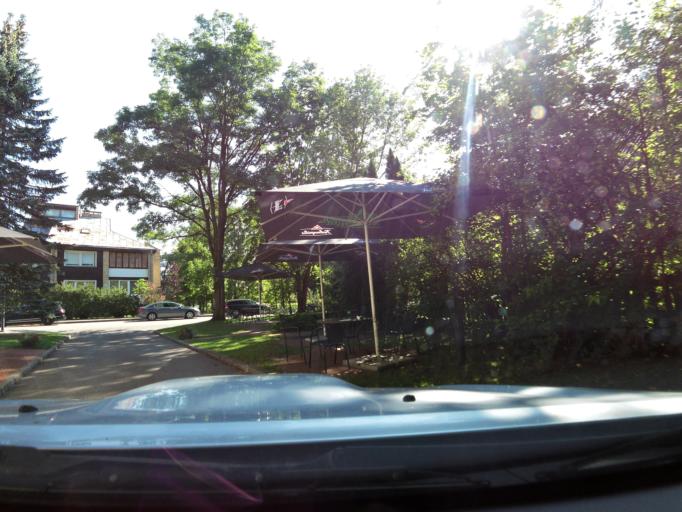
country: LT
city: Birstonas
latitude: 54.6054
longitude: 24.0246
